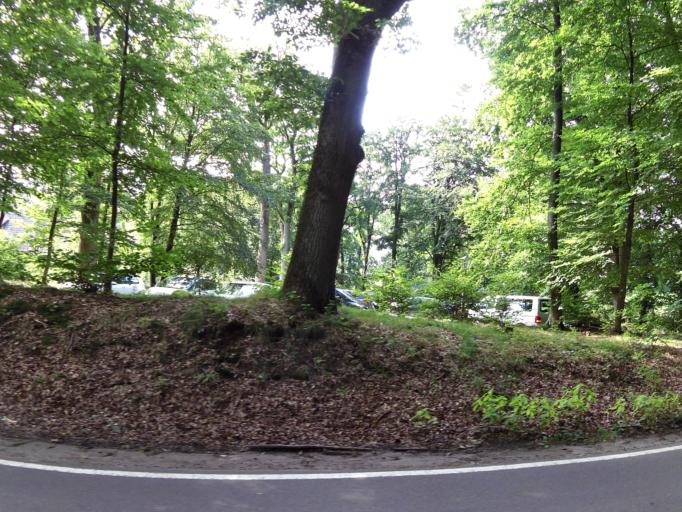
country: DE
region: Lower Saxony
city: Undeloh
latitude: 53.1495
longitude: 9.9088
